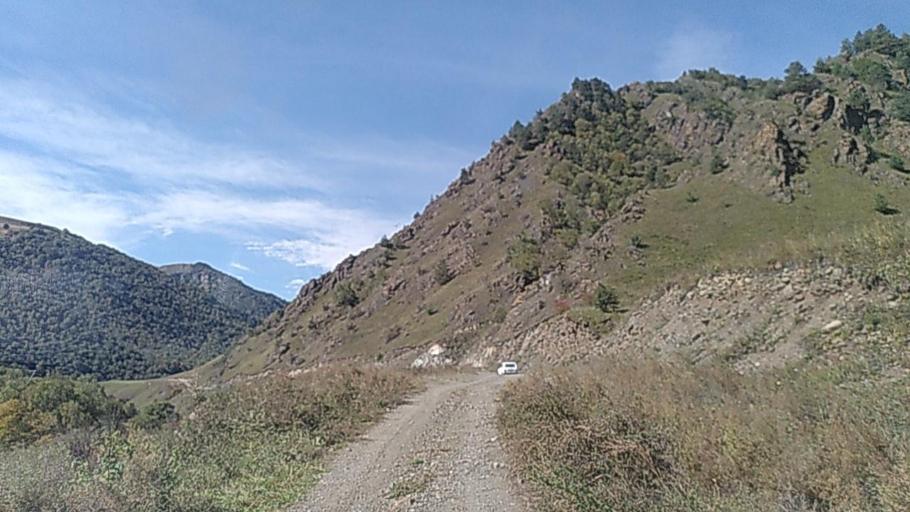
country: RU
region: Kabardino-Balkariya
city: Kamennomostskoye
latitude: 43.7224
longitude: 42.8475
